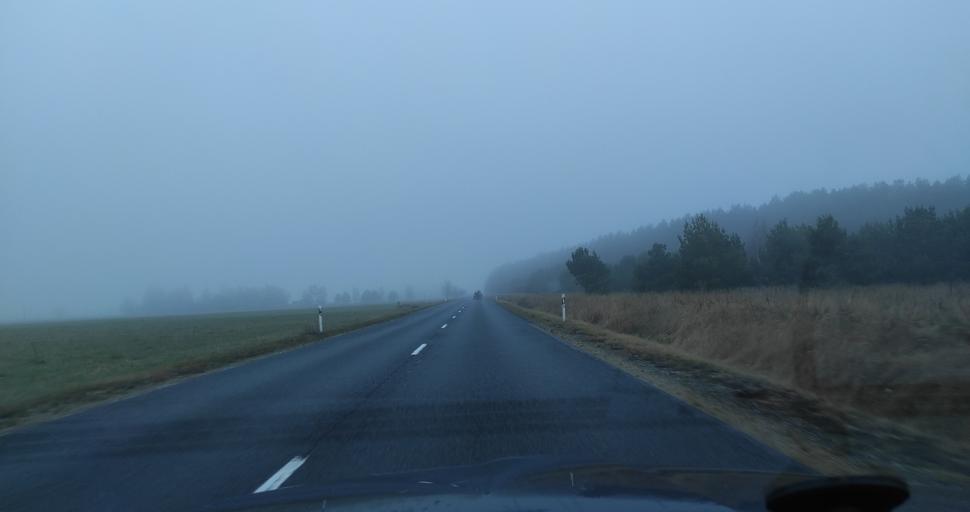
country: LV
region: Alsunga
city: Alsunga
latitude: 57.1099
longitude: 21.4228
